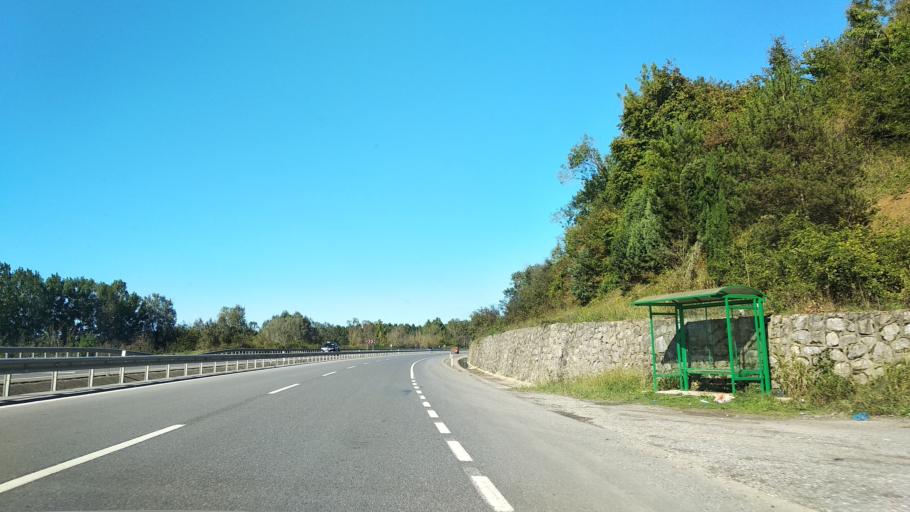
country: TR
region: Sakarya
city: Ortakoy
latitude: 41.0348
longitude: 30.6173
